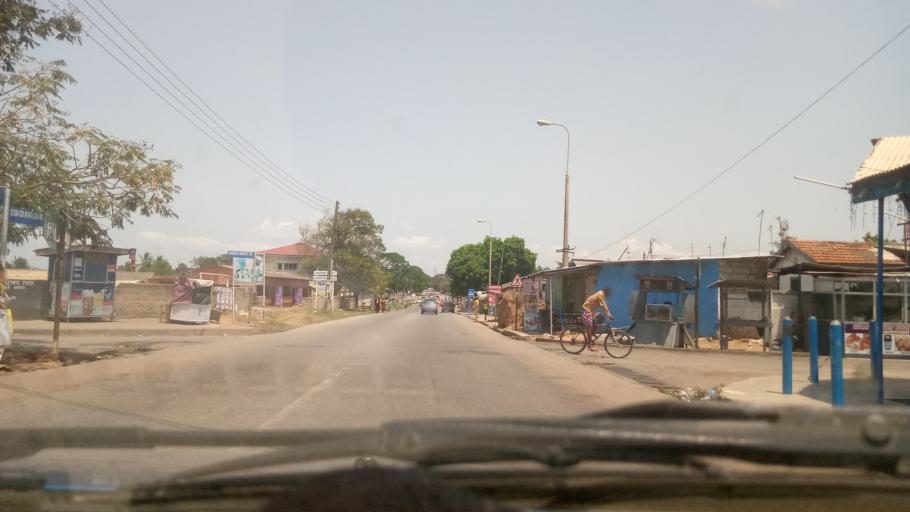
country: GH
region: Greater Accra
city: Accra
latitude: 5.5368
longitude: -0.2383
